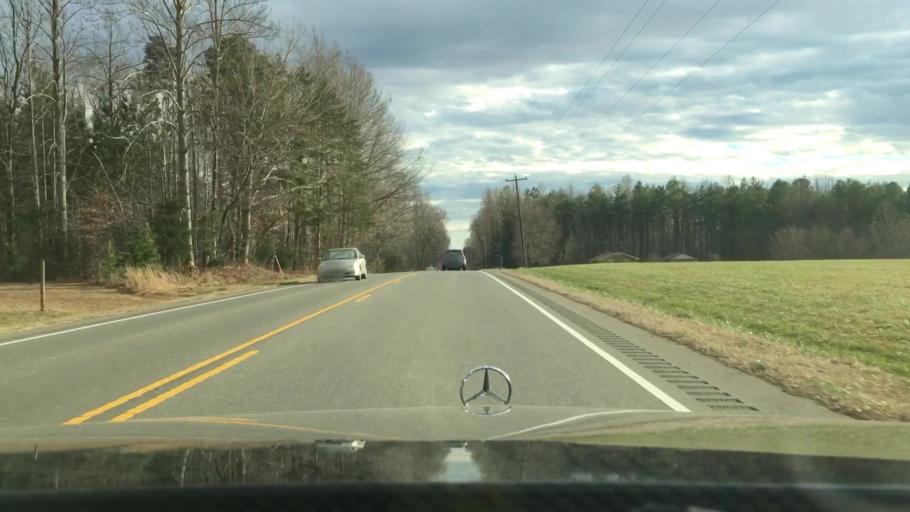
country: US
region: North Carolina
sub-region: Orange County
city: Hillsborough
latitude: 36.1891
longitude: -79.1385
